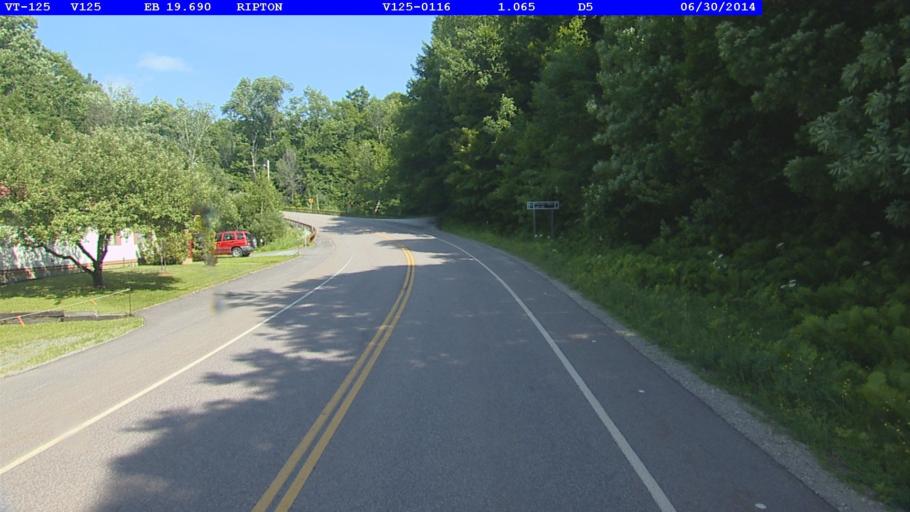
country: US
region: Vermont
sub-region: Addison County
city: Middlebury (village)
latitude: 43.9742
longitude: -73.0409
